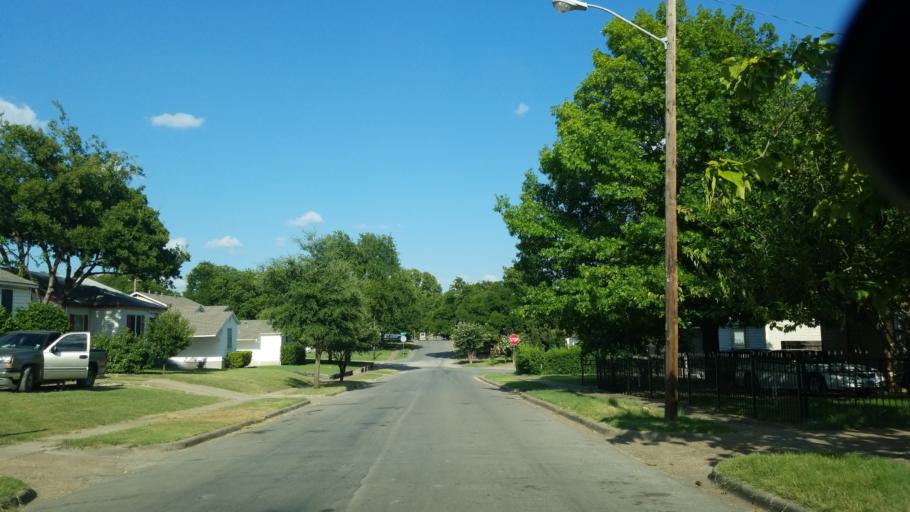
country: US
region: Texas
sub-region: Dallas County
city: Balch Springs
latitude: 32.7673
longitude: -96.7065
